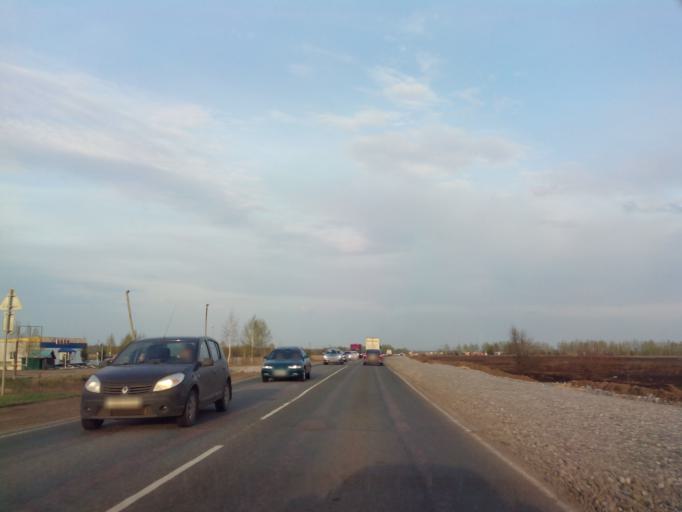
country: RU
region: Rjazan
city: Korablino
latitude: 53.7520
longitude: 39.8367
